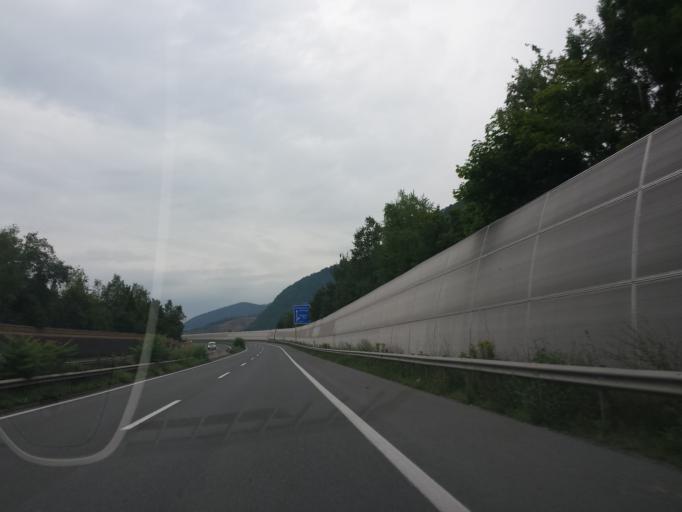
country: AT
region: Styria
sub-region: Politischer Bezirk Graz-Umgebung
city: Peggau
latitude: 47.1978
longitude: 15.3456
